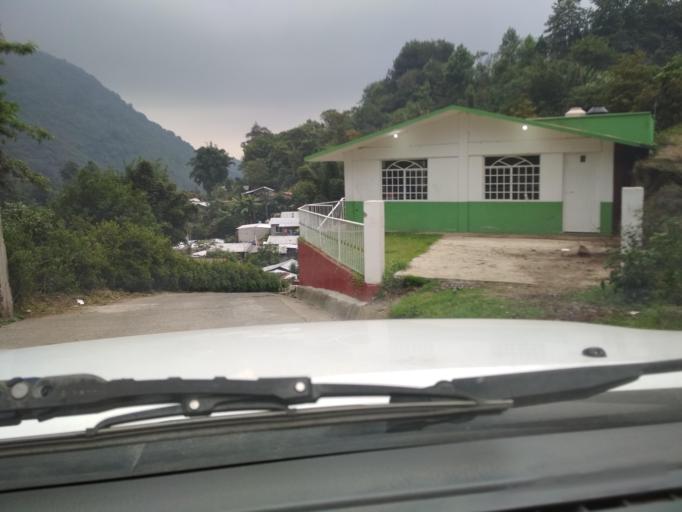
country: MX
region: Veracruz
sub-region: La Perla
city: Barrio de San Miguel
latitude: 18.9298
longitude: -97.1258
